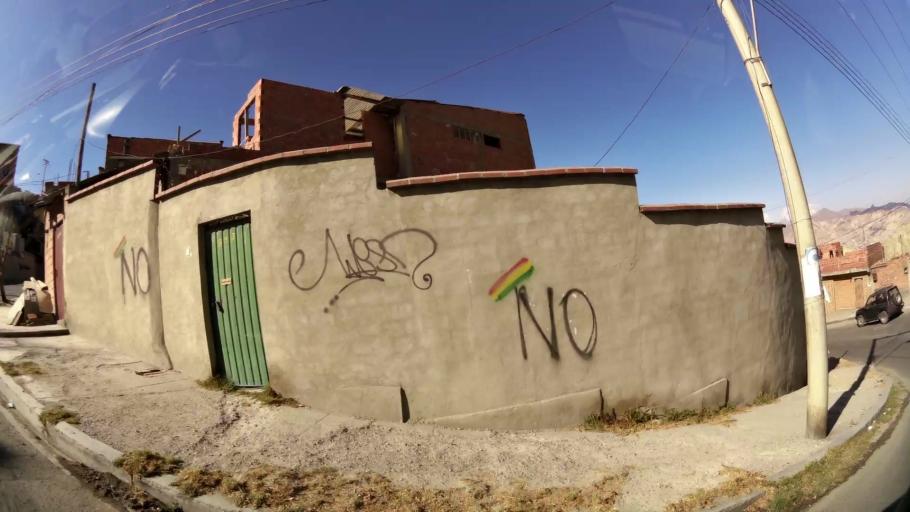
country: BO
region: La Paz
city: La Paz
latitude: -16.5204
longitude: -68.1275
